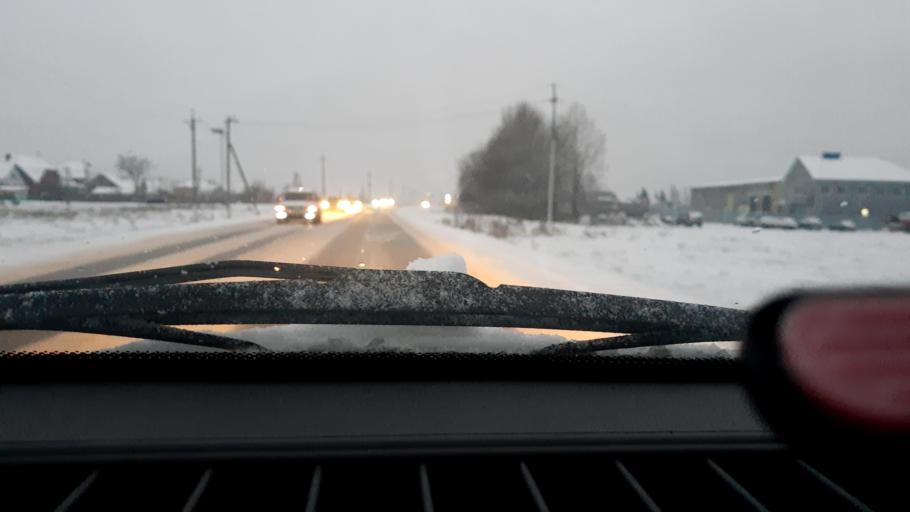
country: RU
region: Bashkortostan
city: Mikhaylovka
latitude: 54.8252
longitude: 55.8884
